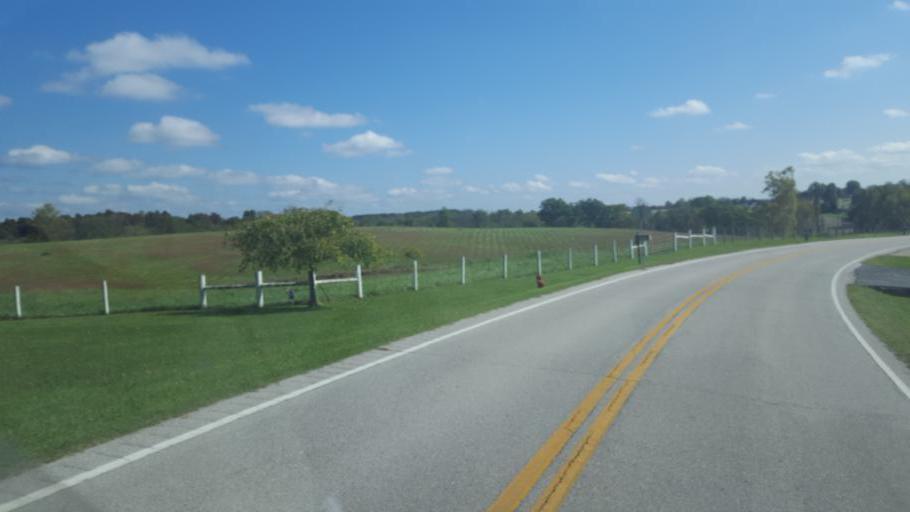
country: US
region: Ohio
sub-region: Adams County
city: Manchester
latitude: 38.5738
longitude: -83.6420
